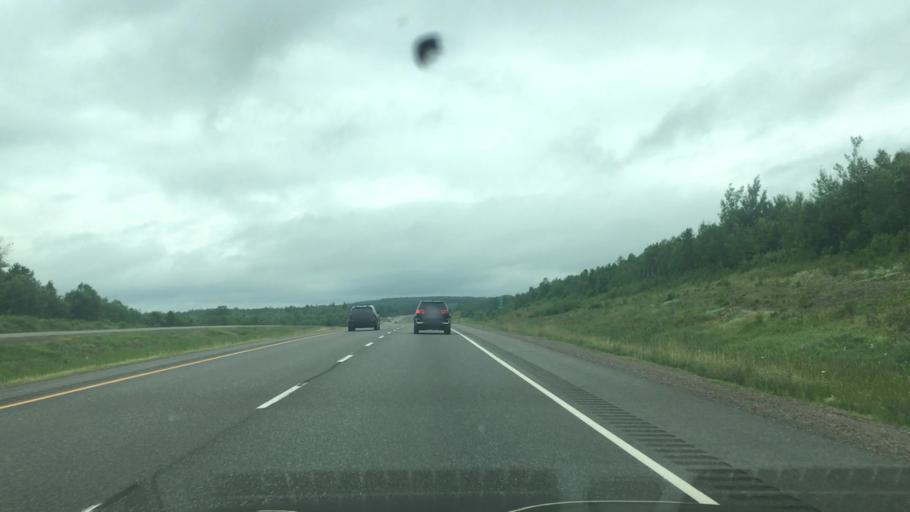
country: CA
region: Nova Scotia
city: Truro
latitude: 45.4510
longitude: -63.6219
